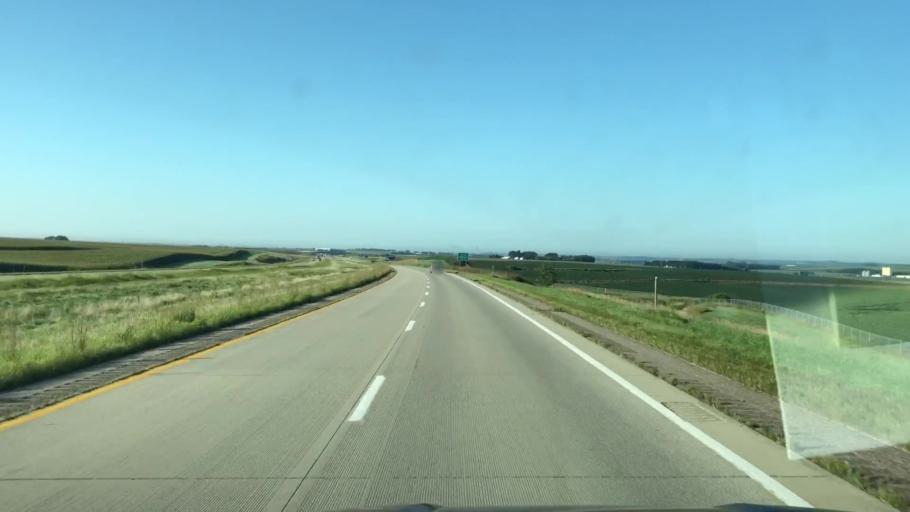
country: US
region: Iowa
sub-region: Plymouth County
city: Le Mars
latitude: 42.8075
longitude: -96.1984
